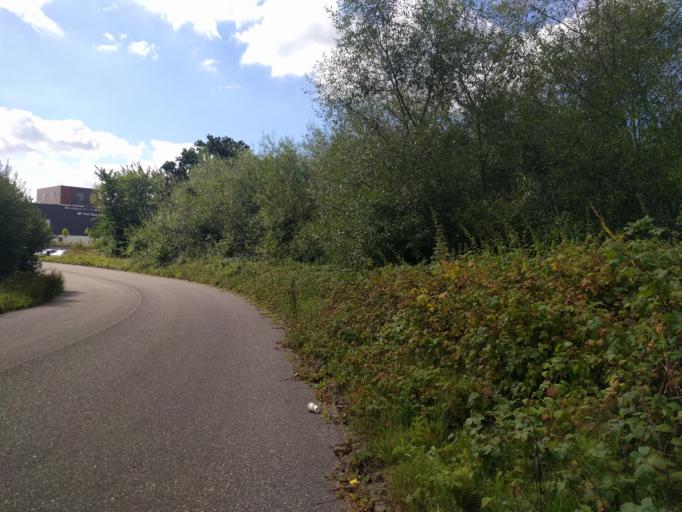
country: DK
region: South Denmark
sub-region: Fredericia Kommune
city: Snoghoj
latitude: 55.5300
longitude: 9.7245
